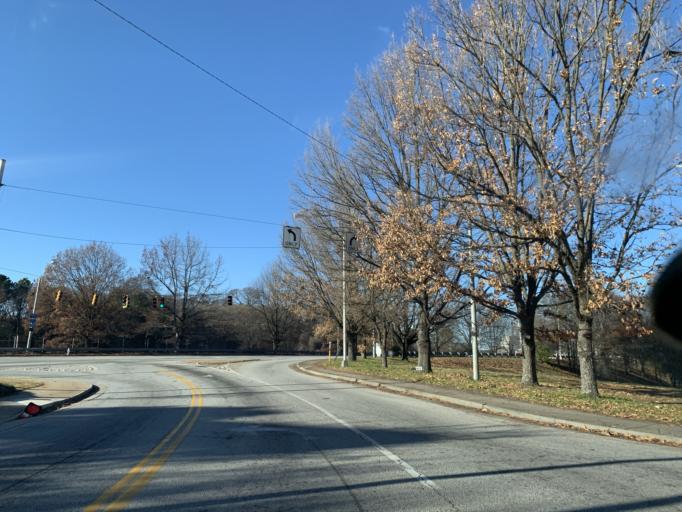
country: US
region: Georgia
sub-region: Fulton County
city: Atlanta
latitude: 33.7270
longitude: -84.3924
